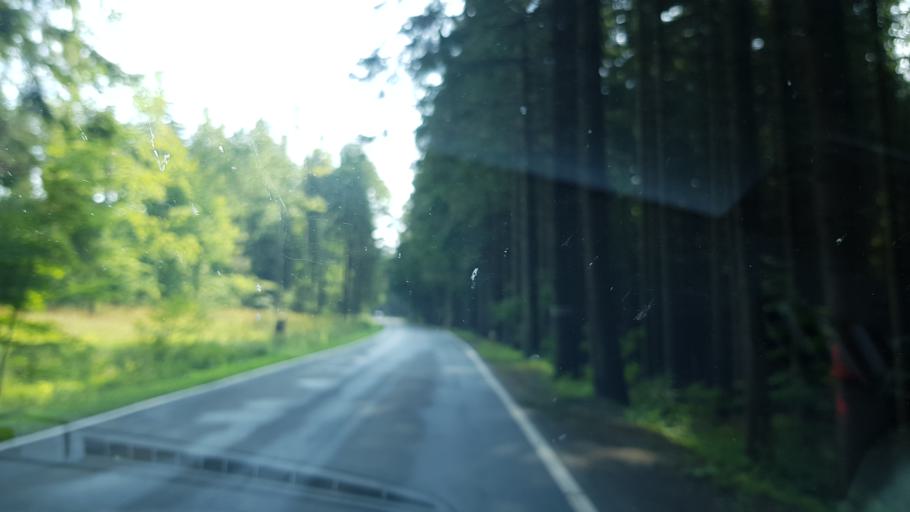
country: CZ
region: Olomoucky
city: Ceska Ves
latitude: 50.2186
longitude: 17.2668
